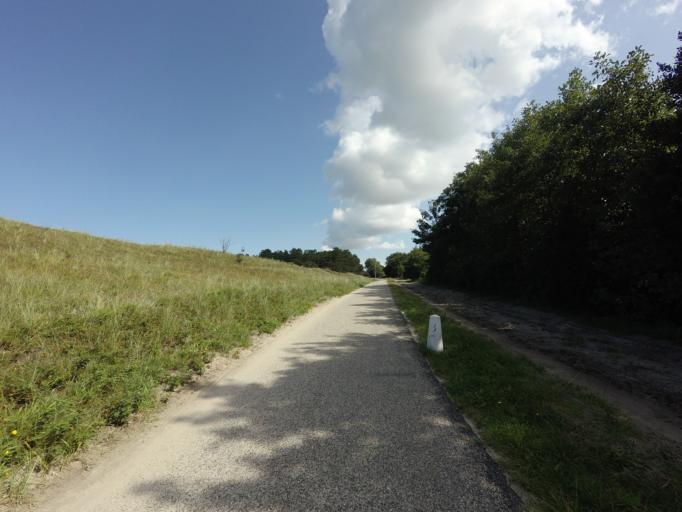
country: NL
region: Friesland
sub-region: Gemeente Terschelling
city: West-Terschelling
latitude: 53.3978
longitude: 5.3349
